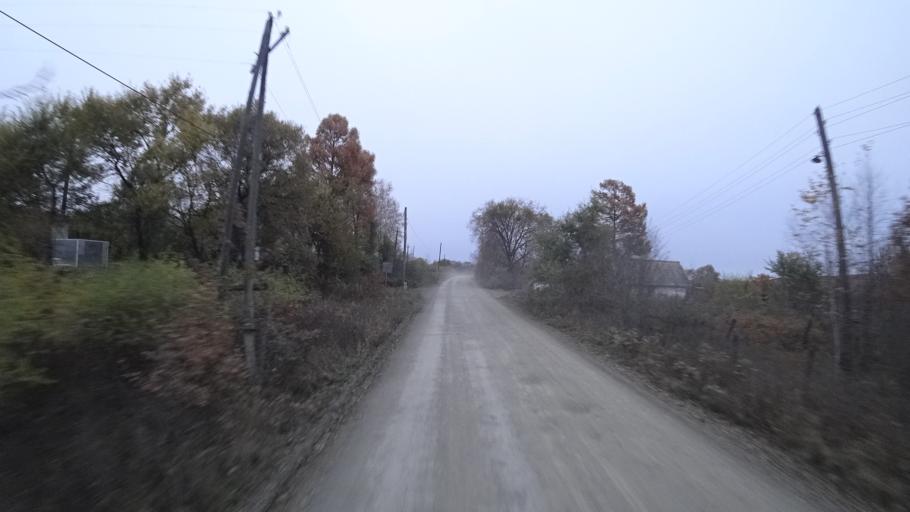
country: RU
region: Khabarovsk Krai
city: Amursk
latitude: 49.9014
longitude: 136.1424
